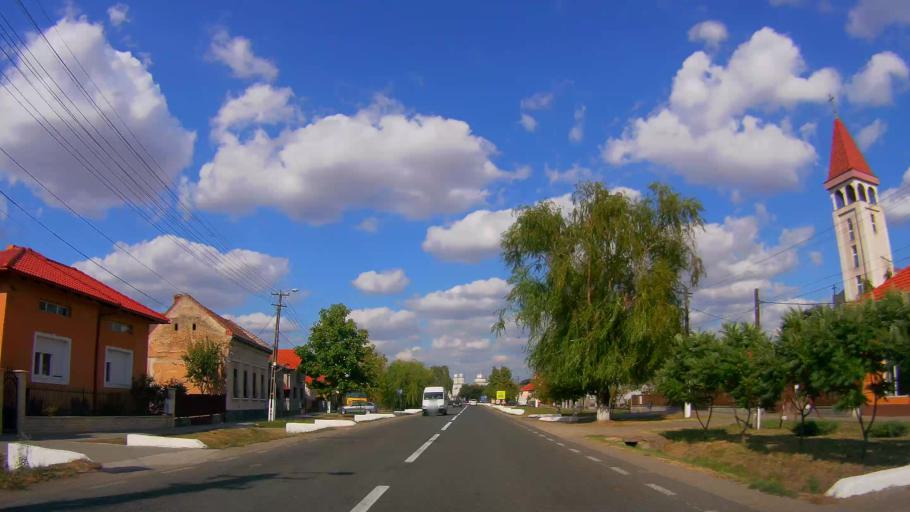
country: RO
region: Satu Mare
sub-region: Oras Ardud
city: Ardud
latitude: 47.6424
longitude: 22.8902
